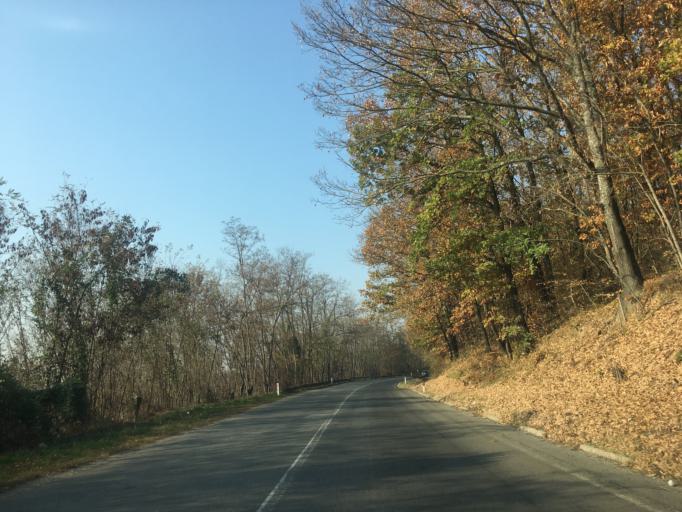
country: XK
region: Pec
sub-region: Komuna e Pejes
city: Kosuriq
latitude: 42.6385
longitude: 20.4310
